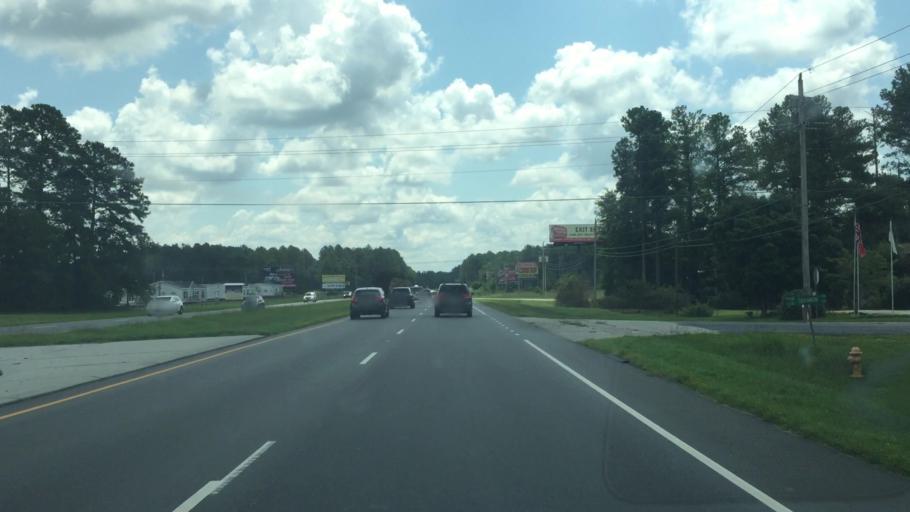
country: US
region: North Carolina
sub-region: Scotland County
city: Laurel Hill
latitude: 34.8051
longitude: -79.5418
